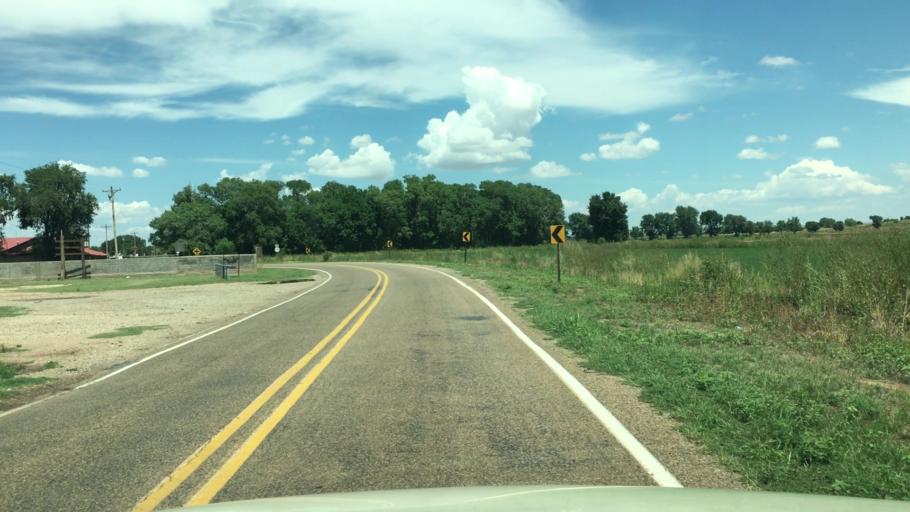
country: US
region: New Mexico
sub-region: De Baca County
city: Fort Sumner
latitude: 34.4028
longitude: -104.1931
